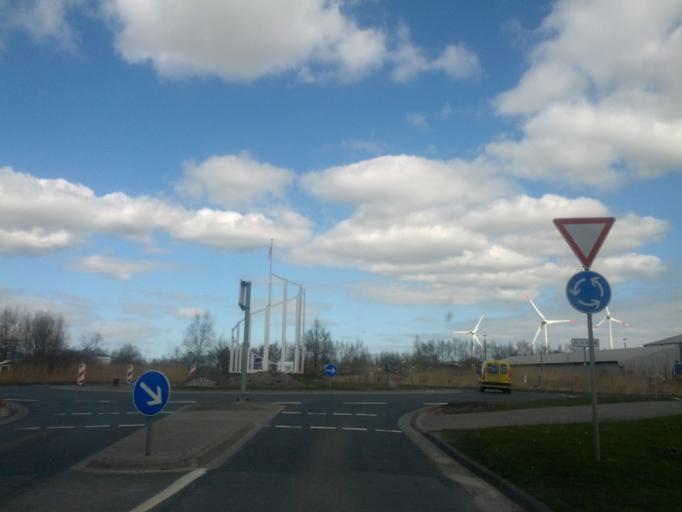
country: DE
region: Lower Saxony
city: Wittmund
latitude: 53.5785
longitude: 7.8008
